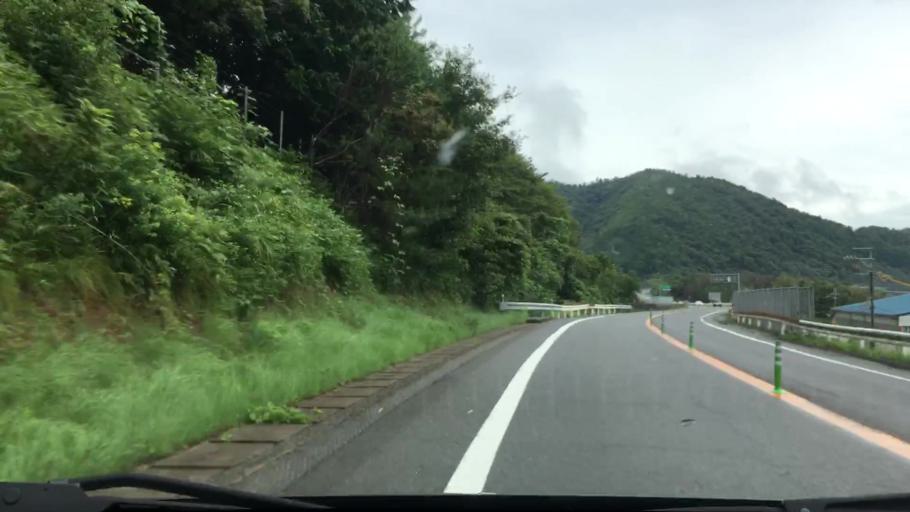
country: JP
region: Hyogo
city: Himeji
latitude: 35.0078
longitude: 134.7639
